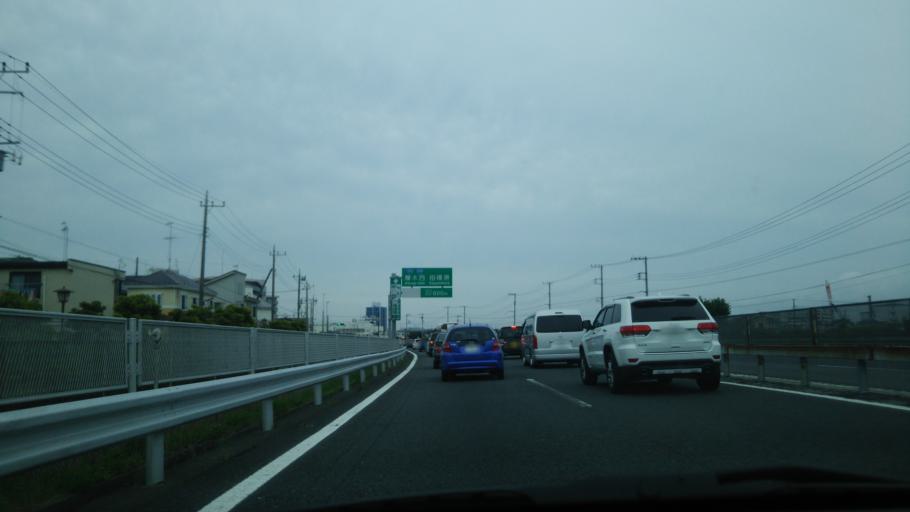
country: JP
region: Kanagawa
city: Atsugi
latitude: 35.4092
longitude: 139.3443
